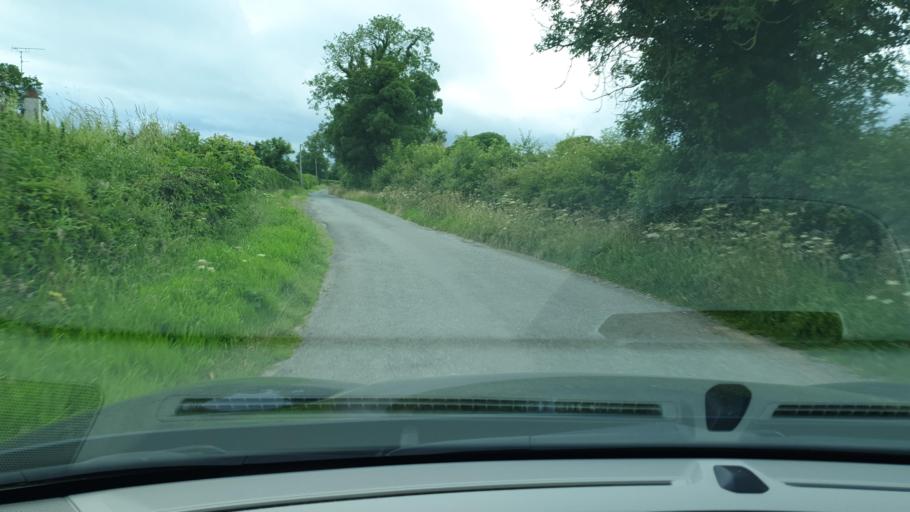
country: IE
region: Leinster
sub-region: An Mhi
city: Dunshaughlin
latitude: 53.5365
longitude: -6.5164
